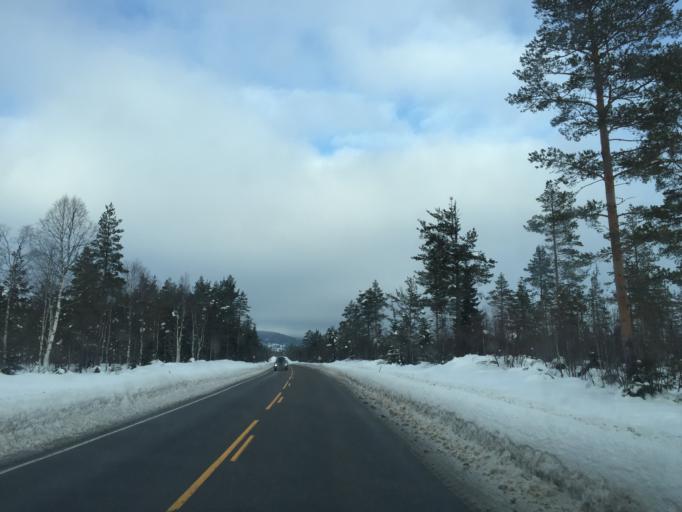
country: NO
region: Hedmark
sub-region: Trysil
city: Innbygda
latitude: 61.1451
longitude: 12.1254
